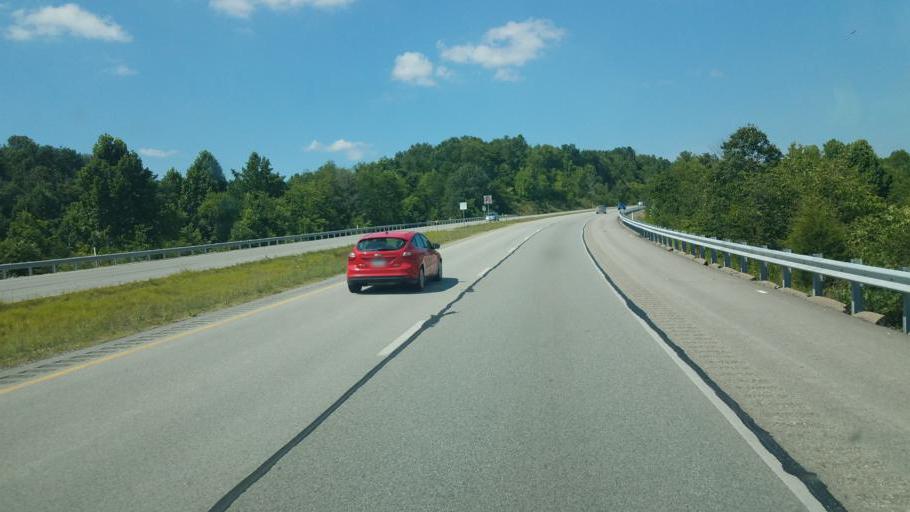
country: US
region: West Virginia
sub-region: Kanawha County
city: Sissonville
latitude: 38.6595
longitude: -81.6532
